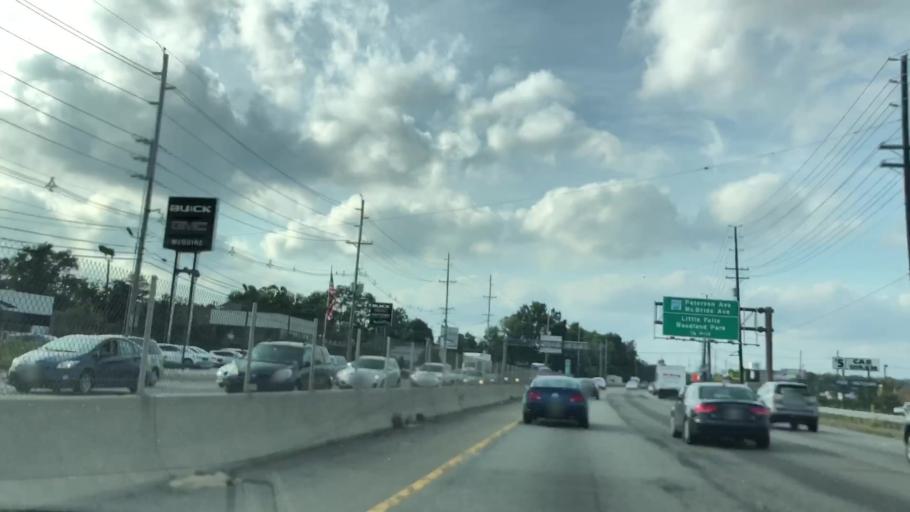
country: US
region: New Jersey
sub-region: Passaic County
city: Little Falls
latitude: 40.8852
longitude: -74.2142
